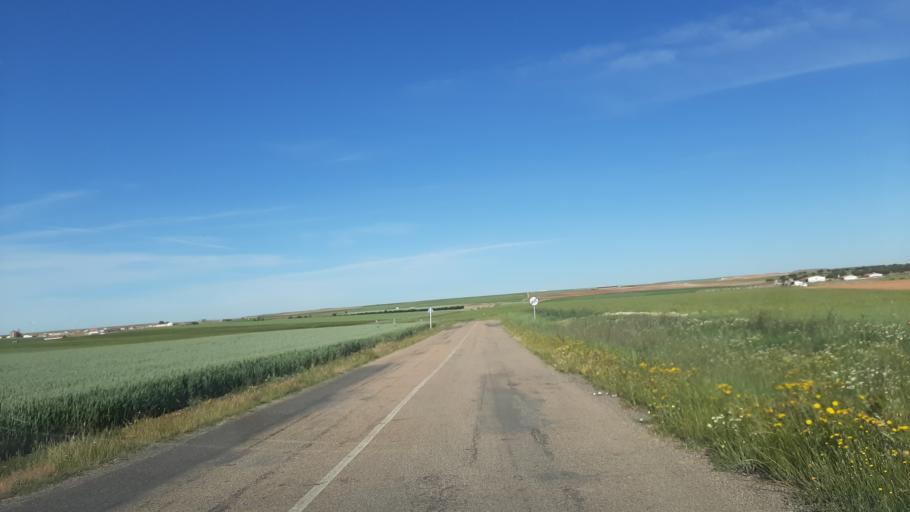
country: ES
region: Castille and Leon
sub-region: Provincia de Salamanca
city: Aldeaseca de Alba
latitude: 40.8251
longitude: -5.4283
